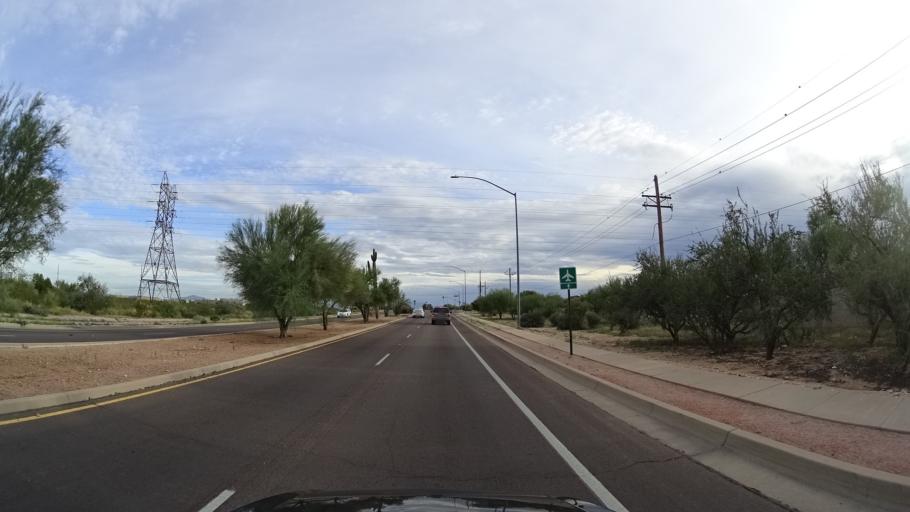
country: US
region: Arizona
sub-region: Pima County
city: South Tucson
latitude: 32.1506
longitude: -110.9351
